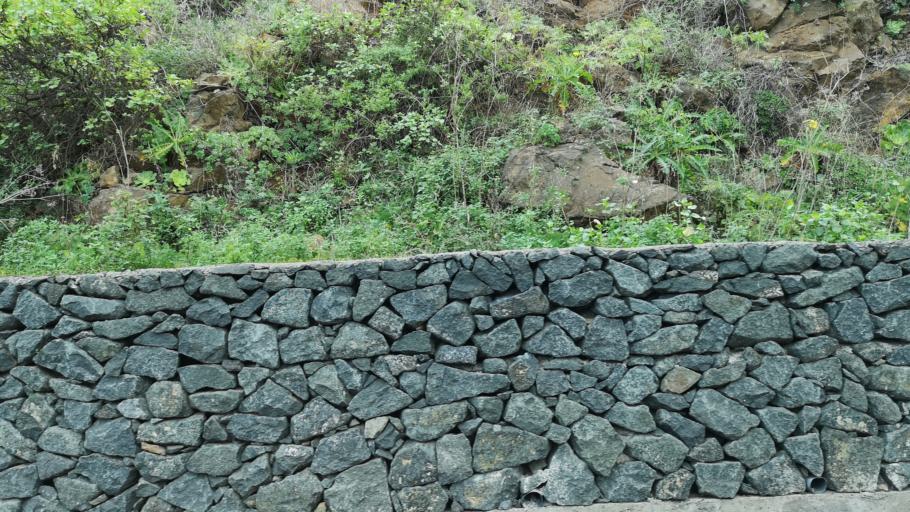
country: ES
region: Canary Islands
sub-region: Provincia de Santa Cruz de Tenerife
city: Agulo
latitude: 28.1870
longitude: -17.2135
